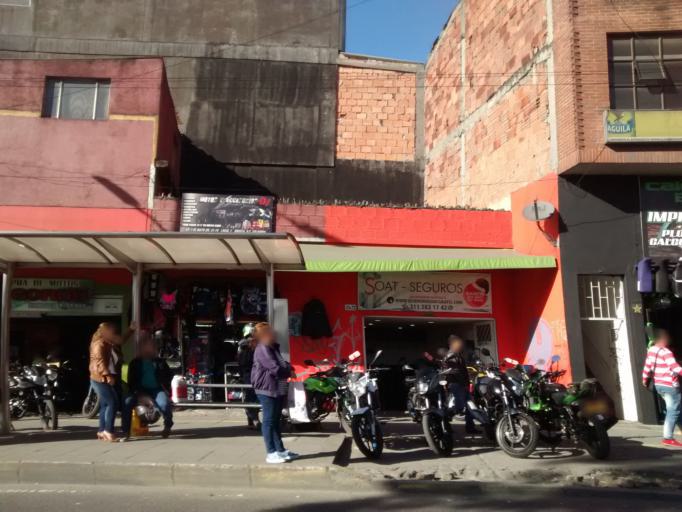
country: CO
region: Bogota D.C.
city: Bogota
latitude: 4.5930
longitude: -74.1115
